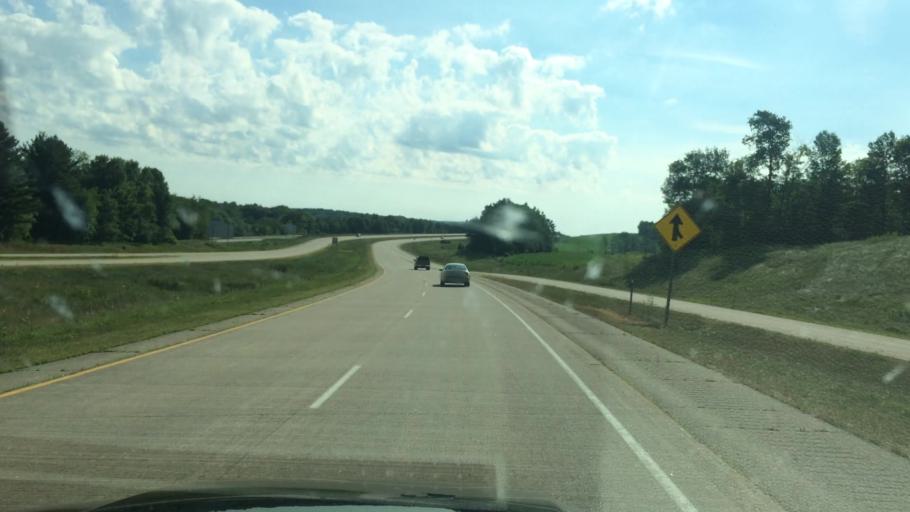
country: US
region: Wisconsin
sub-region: Shawano County
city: Wittenberg
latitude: 44.8244
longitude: -89.1192
